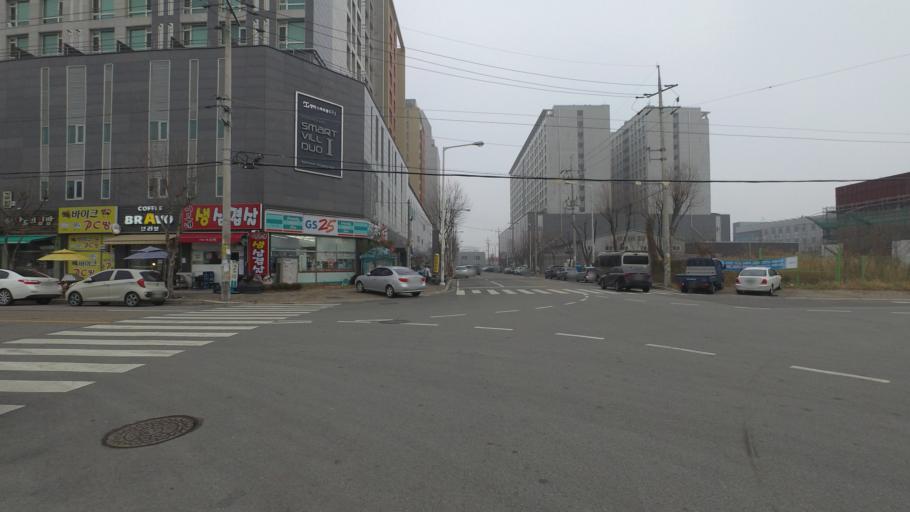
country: KR
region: Chungcheongnam-do
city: Tangjin
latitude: 36.9755
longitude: 126.8442
